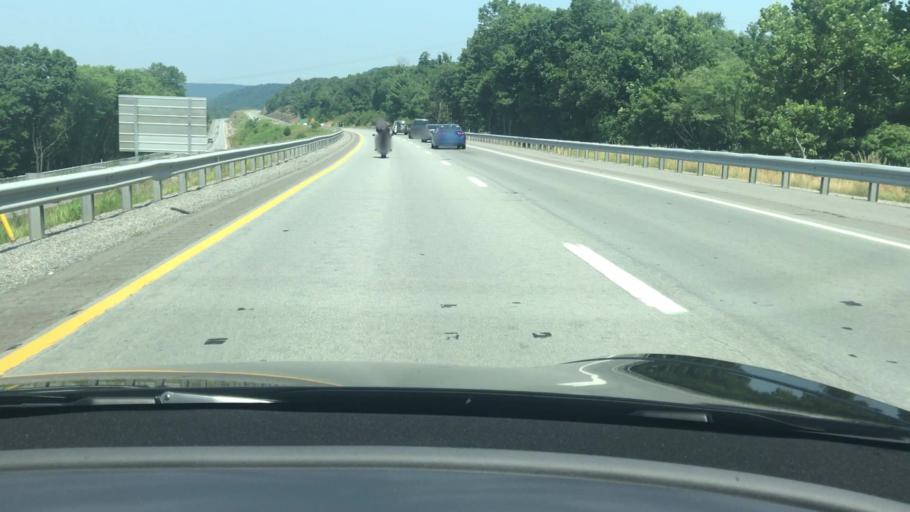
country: US
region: Pennsylvania
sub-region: Perry County
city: Duncannon
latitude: 40.4433
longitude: -77.0160
